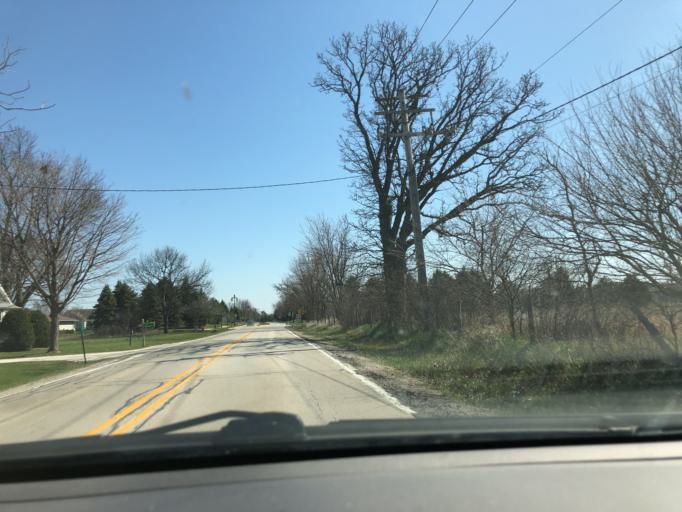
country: US
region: Illinois
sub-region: McHenry County
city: Huntley
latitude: 42.1622
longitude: -88.4565
